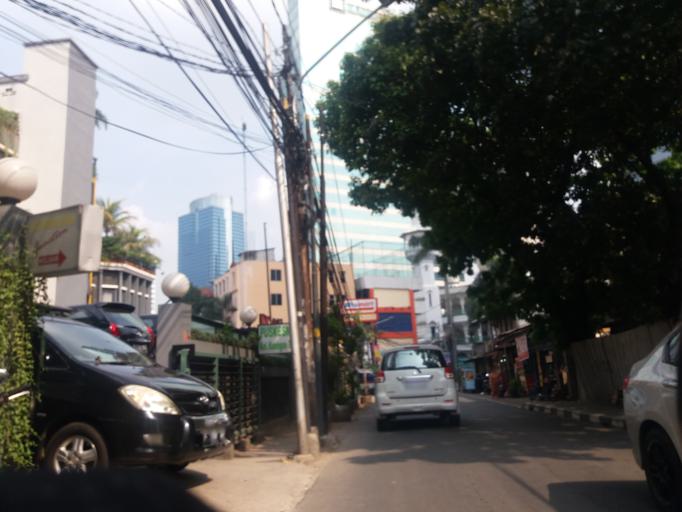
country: ID
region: Jakarta Raya
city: Jakarta
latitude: -6.2300
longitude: 106.8215
